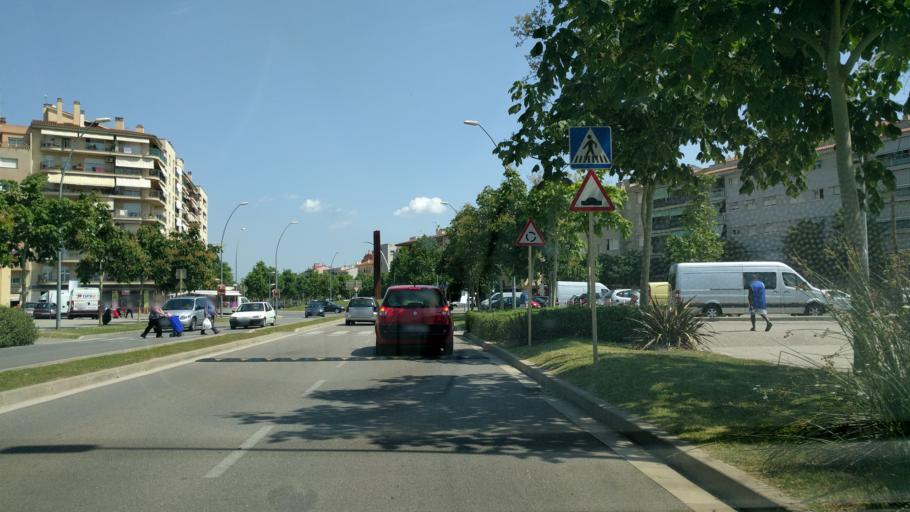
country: ES
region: Catalonia
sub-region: Provincia de Girona
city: Salt
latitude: 41.9734
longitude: 2.8011
